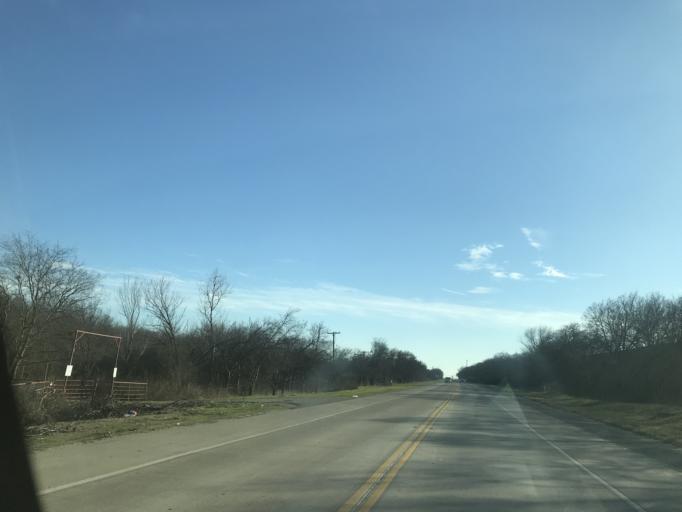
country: US
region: Texas
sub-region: Ellis County
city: Ferris
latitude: 32.5489
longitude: -96.6656
